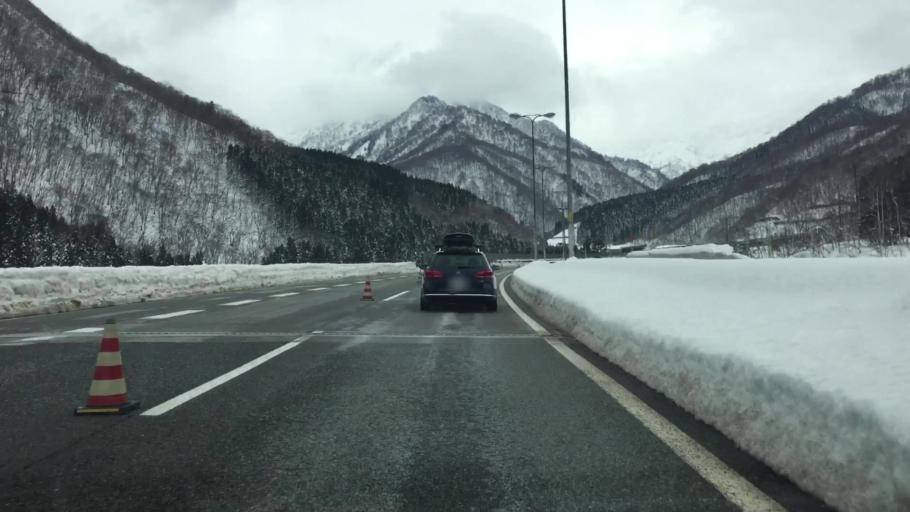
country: JP
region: Niigata
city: Shiozawa
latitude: 36.8753
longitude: 138.8624
